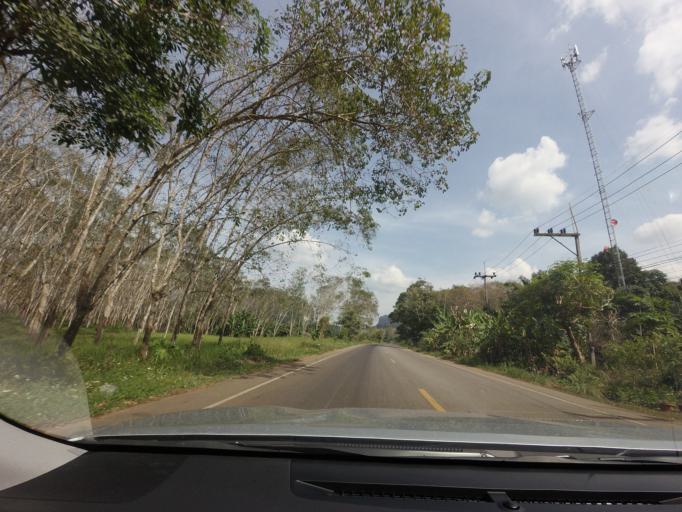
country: TH
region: Phangnga
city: Ban Ao Nang
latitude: 8.1442
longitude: 98.8289
